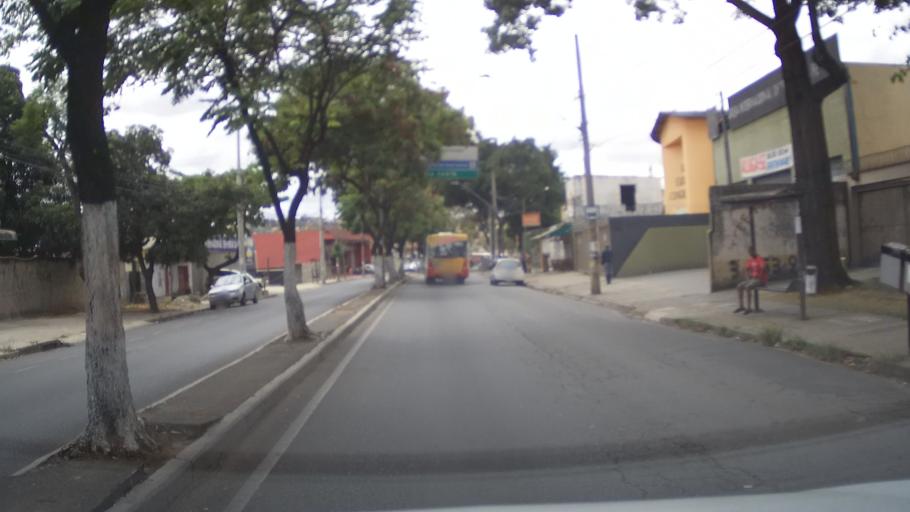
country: BR
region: Minas Gerais
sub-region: Ribeirao Das Neves
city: Ribeirao das Neves
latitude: -19.8040
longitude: -43.9759
